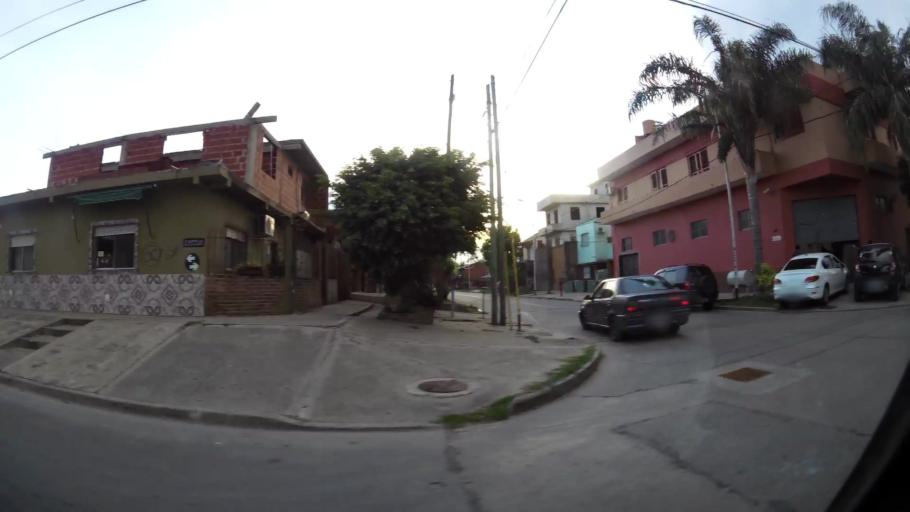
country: AR
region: Buenos Aires
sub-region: Partido de Avellaneda
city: Avellaneda
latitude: -34.6840
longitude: -58.3237
